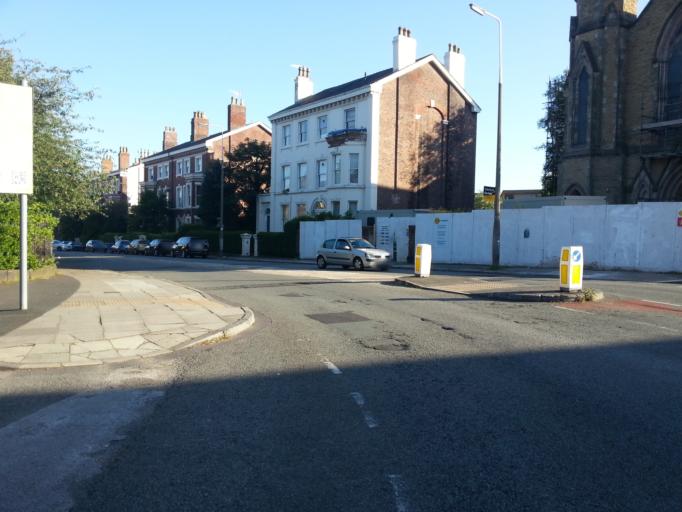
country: GB
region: England
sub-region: Liverpool
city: Liverpool
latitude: 53.3867
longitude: -2.9588
